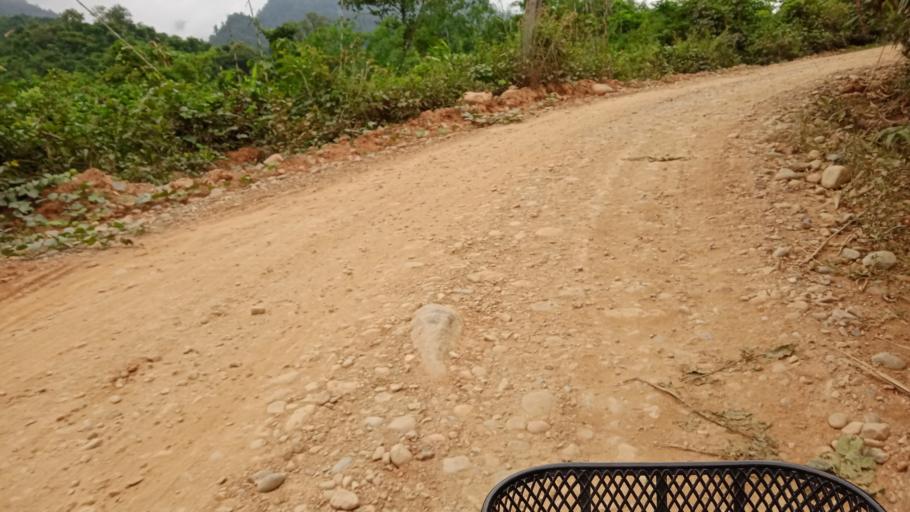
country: LA
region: Xiangkhoang
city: Phonsavan
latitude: 19.0945
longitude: 102.9908
